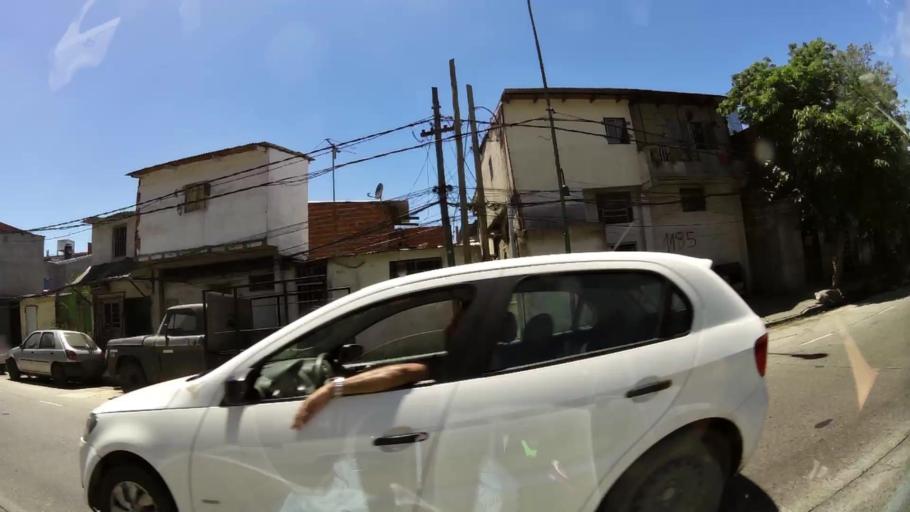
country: AR
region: Buenos Aires
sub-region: Partido de General San Martin
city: General San Martin
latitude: -34.5495
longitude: -58.5250
